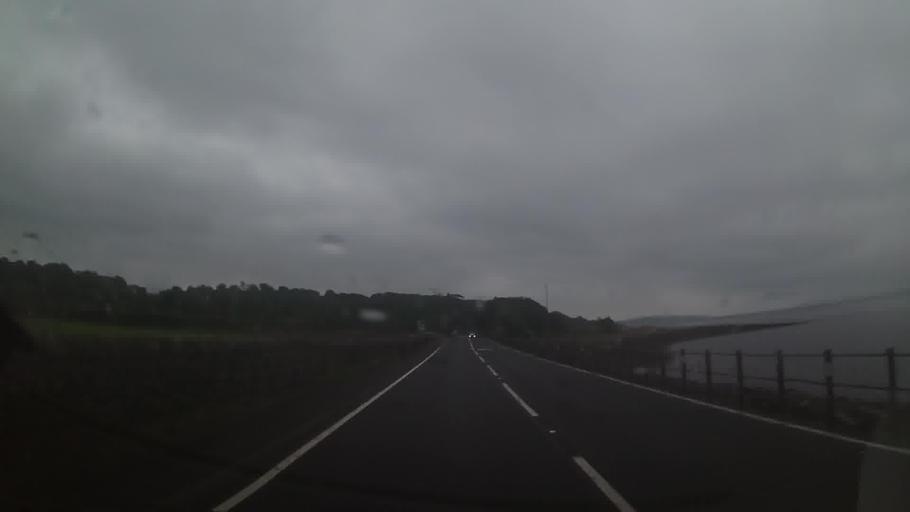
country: GB
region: Scotland
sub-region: North Ayrshire
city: Skelmorlie
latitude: 55.8514
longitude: -4.8888
